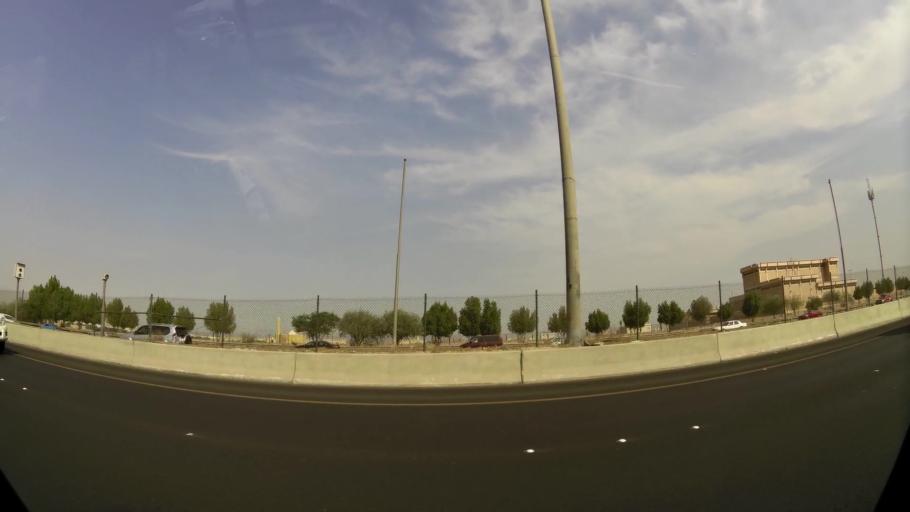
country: KW
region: Al Farwaniyah
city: Janub as Surrah
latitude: 29.2977
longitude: 47.9808
